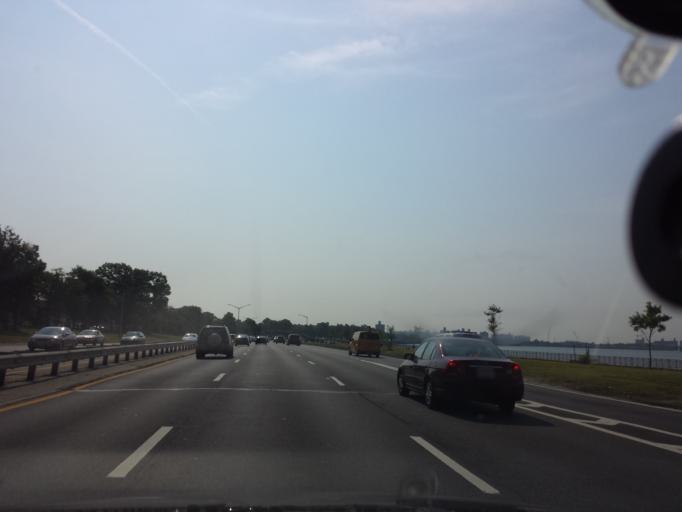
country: US
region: New York
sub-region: Kings County
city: Bensonhurst
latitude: 40.6028
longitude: -74.0163
